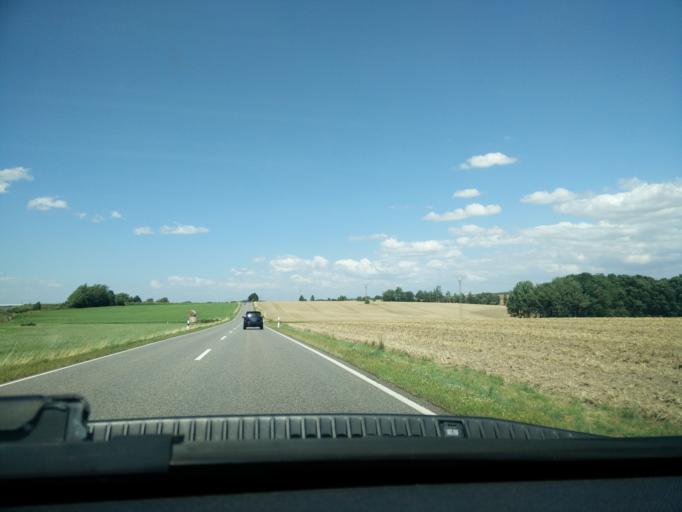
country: DE
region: Saxony
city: Penig
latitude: 50.9769
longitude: 12.6976
